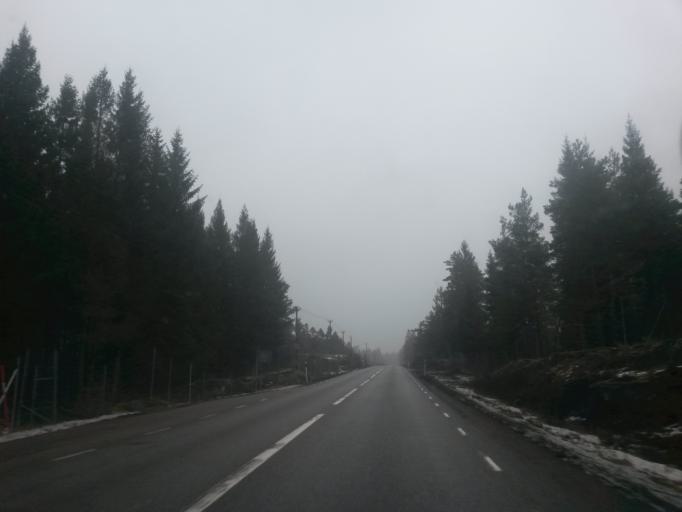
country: SE
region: Vaestra Goetaland
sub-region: Alingsas Kommun
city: Sollebrunn
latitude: 58.1932
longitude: 12.4315
